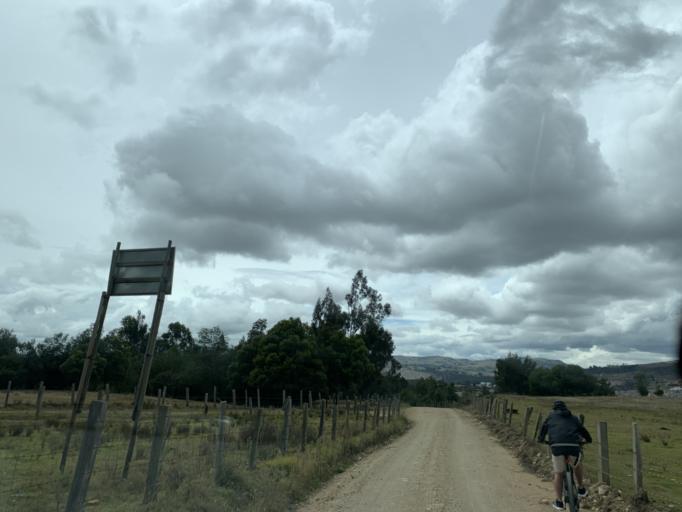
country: CO
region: Boyaca
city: Tunja
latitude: 5.5584
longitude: -73.3250
